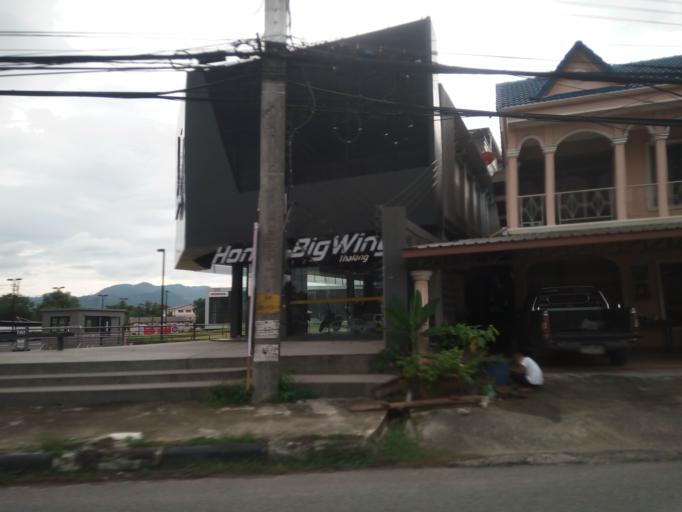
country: TH
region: Phuket
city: Thalang
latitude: 8.0056
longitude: 98.3438
